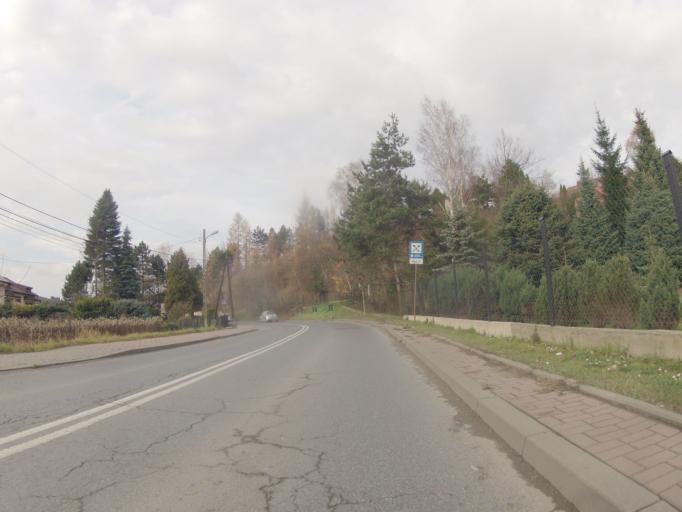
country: PL
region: Lesser Poland Voivodeship
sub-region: Powiat krakowski
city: Rzaska
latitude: 50.0906
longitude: 19.8366
